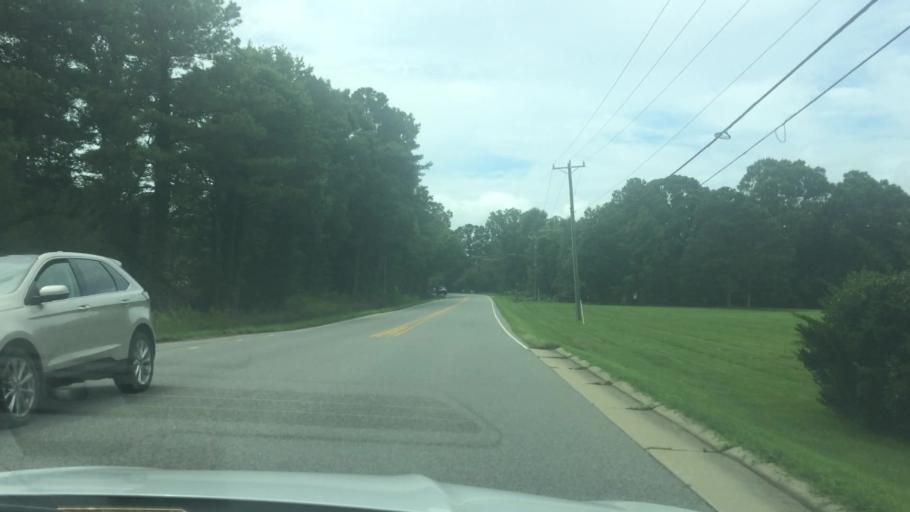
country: US
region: Virginia
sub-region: James City County
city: Williamsburg
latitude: 37.2592
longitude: -76.7643
